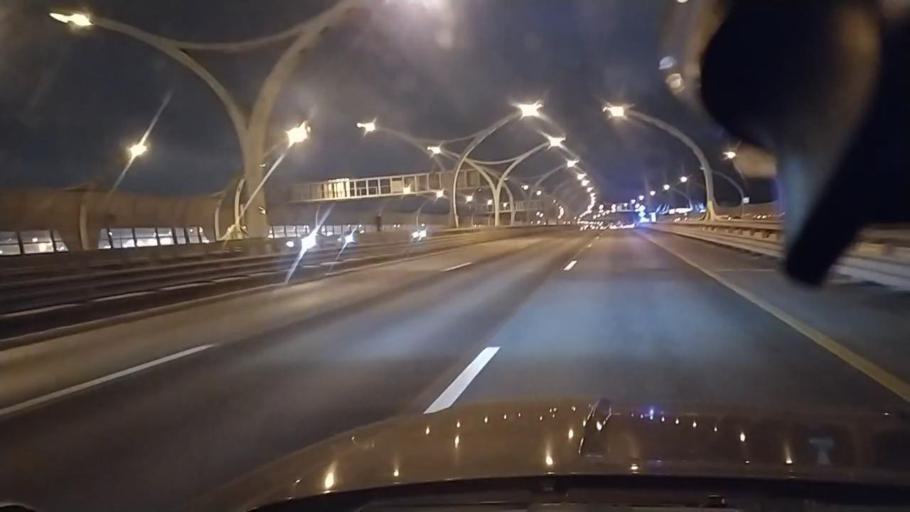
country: RU
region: St.-Petersburg
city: Staraya Derevnya
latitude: 59.9993
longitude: 30.2318
